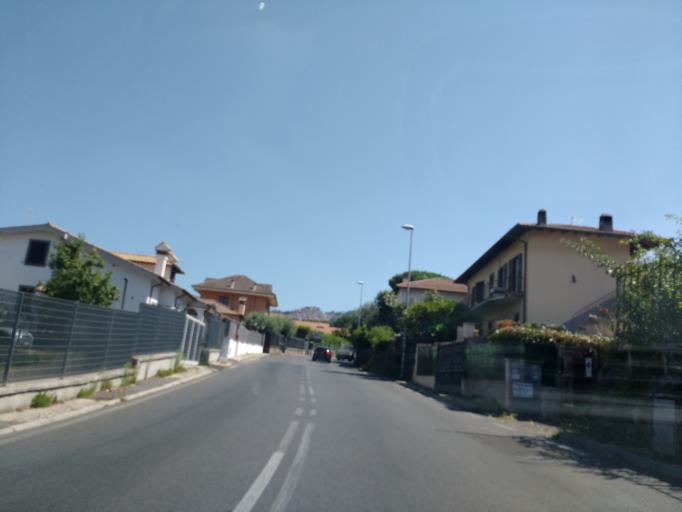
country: IT
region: Latium
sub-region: Citta metropolitana di Roma Capitale
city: Grottaferrata
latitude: 41.7800
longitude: 12.6849
